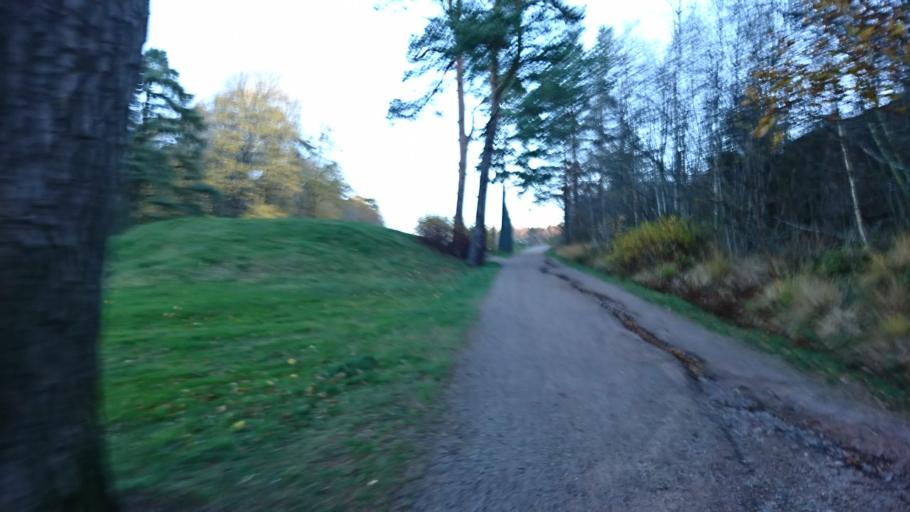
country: SE
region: Vaestra Goetaland
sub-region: Molndal
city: Moelndal
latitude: 57.6885
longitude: 12.0266
